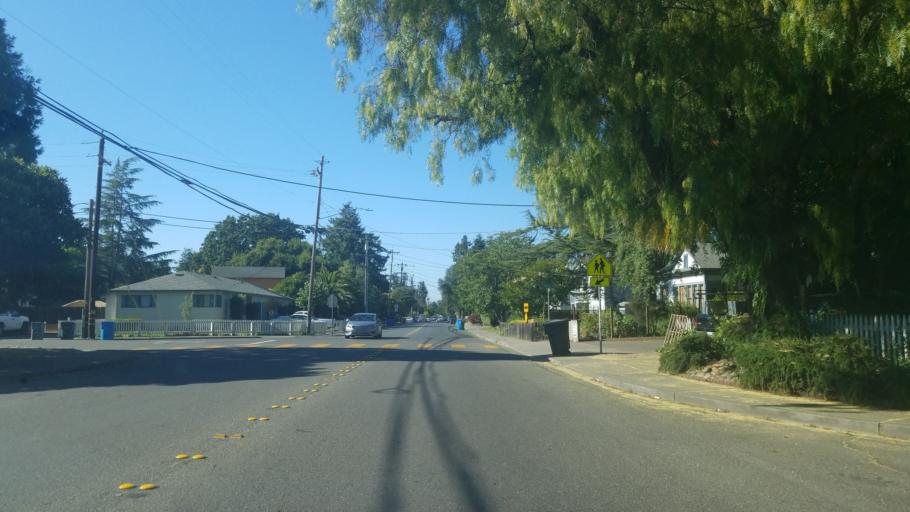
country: US
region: California
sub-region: Sonoma County
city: Roseland
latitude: 38.4238
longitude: -122.7246
